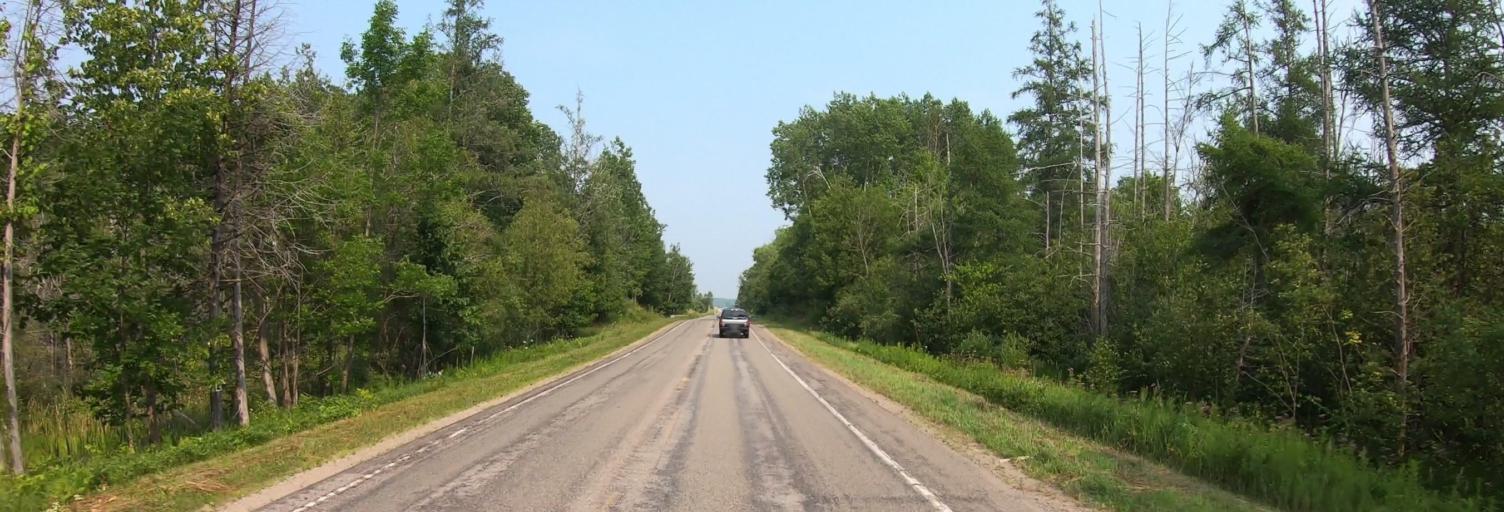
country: US
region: Michigan
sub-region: Charlevoix County
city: Charlevoix
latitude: 45.1842
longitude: -85.2719
